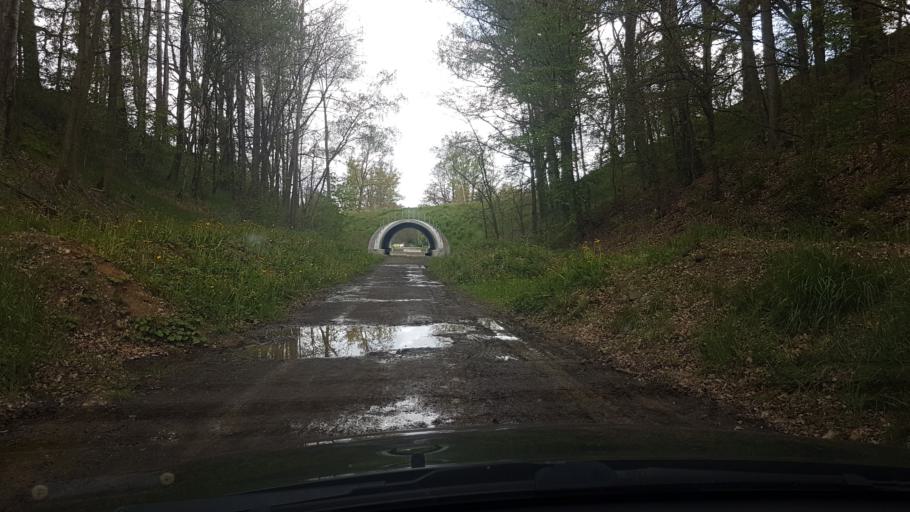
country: CZ
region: Karlovarsky
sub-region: Okres Cheb
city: Cheb
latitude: 50.0514
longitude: 12.3878
